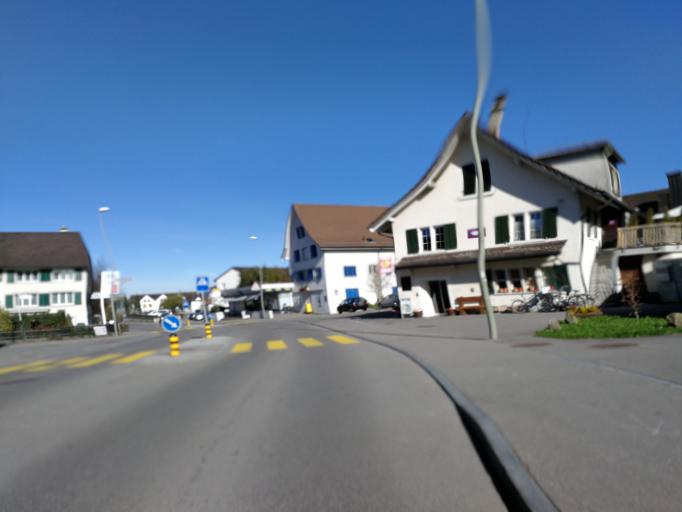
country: CH
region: Zurich
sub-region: Bezirk Hinwil
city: Binzikon
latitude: 47.2781
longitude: 8.7594
